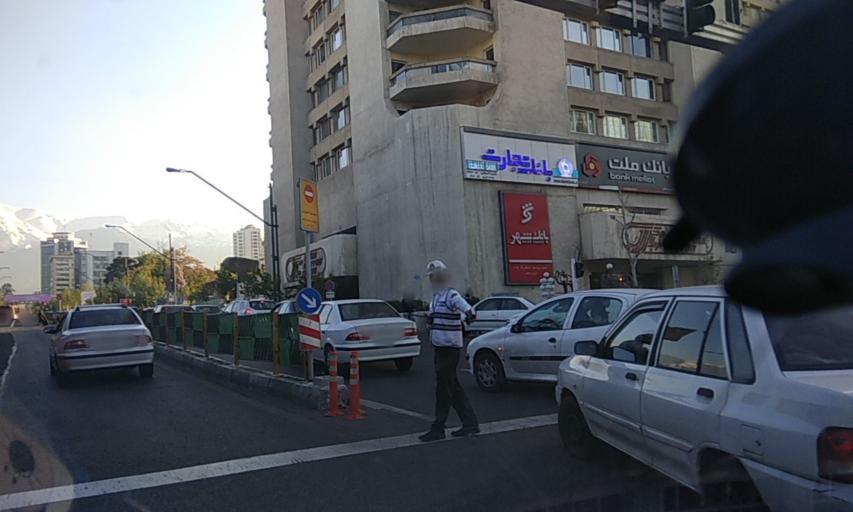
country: IR
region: Tehran
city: Tajrish
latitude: 35.7632
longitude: 51.4101
